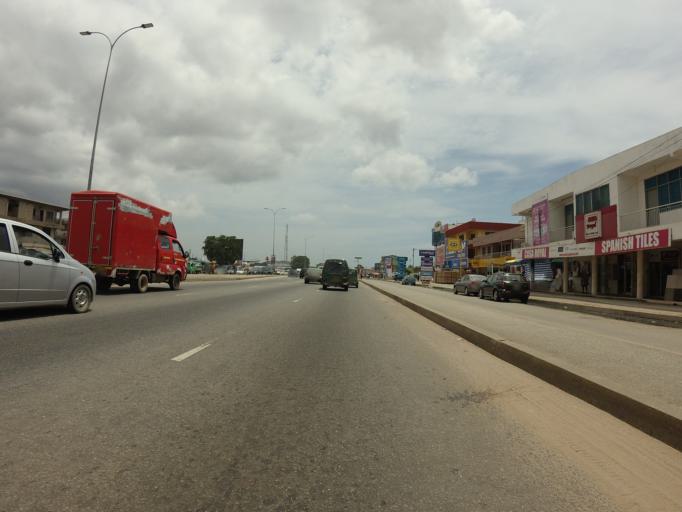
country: GH
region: Greater Accra
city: Gbawe
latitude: 5.5773
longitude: -0.2562
